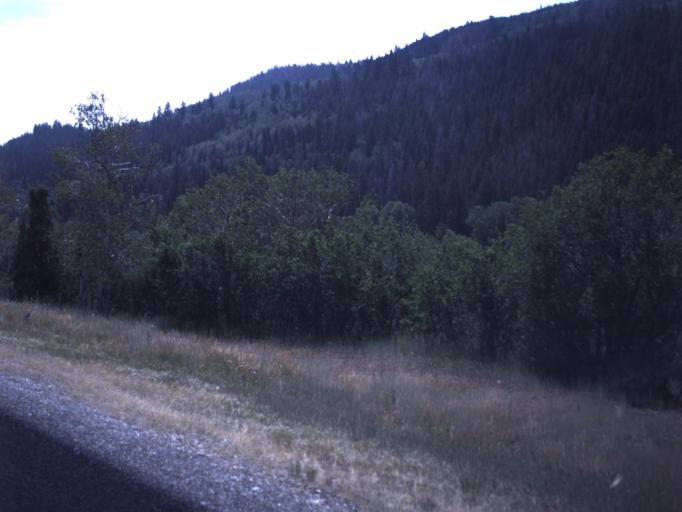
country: US
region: Utah
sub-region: Summit County
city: Francis
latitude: 40.5559
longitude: -111.1117
